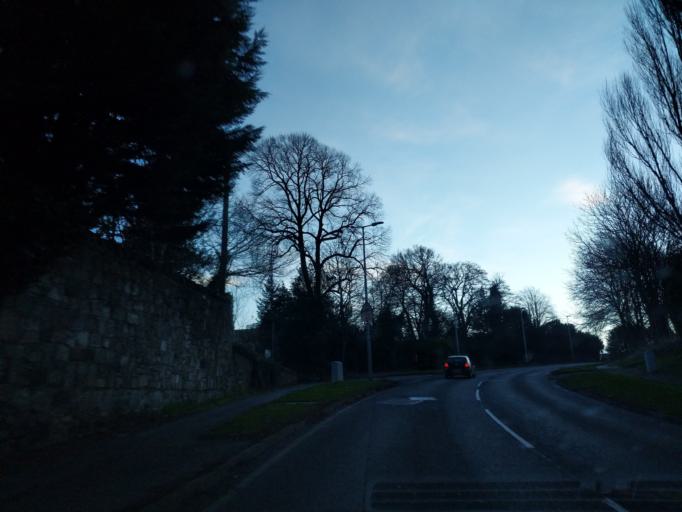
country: GB
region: Scotland
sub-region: Midlothian
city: Bonnyrigg
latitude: 55.8821
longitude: -3.1253
